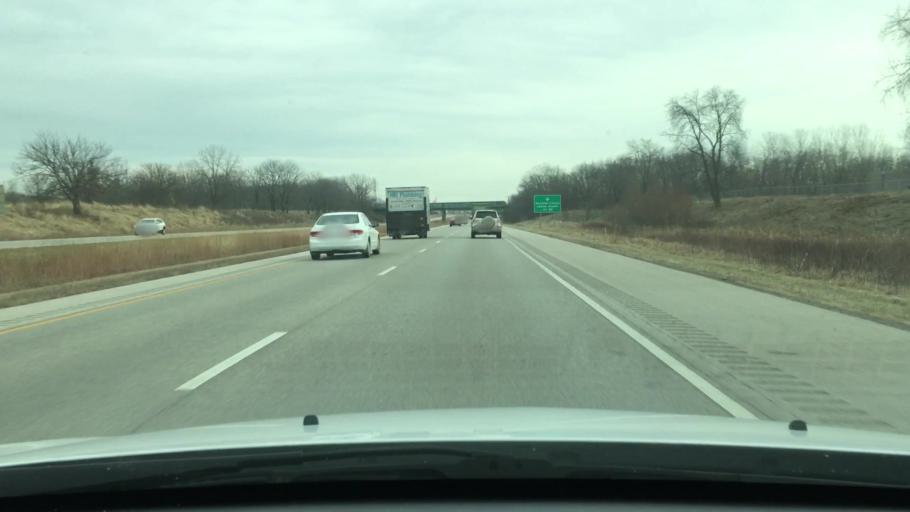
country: US
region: Illinois
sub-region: Sangamon County
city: Jerome
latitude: 39.7460
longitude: -89.7175
